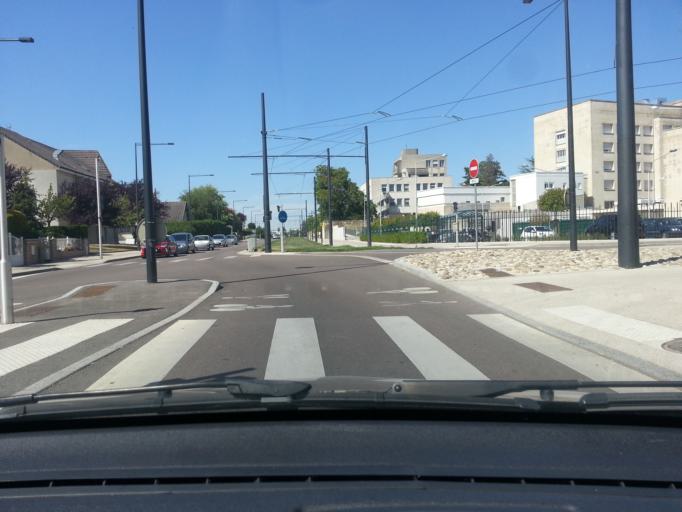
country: FR
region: Bourgogne
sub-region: Departement de la Cote-d'Or
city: Saint-Apollinaire
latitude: 47.3200
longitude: 5.0654
